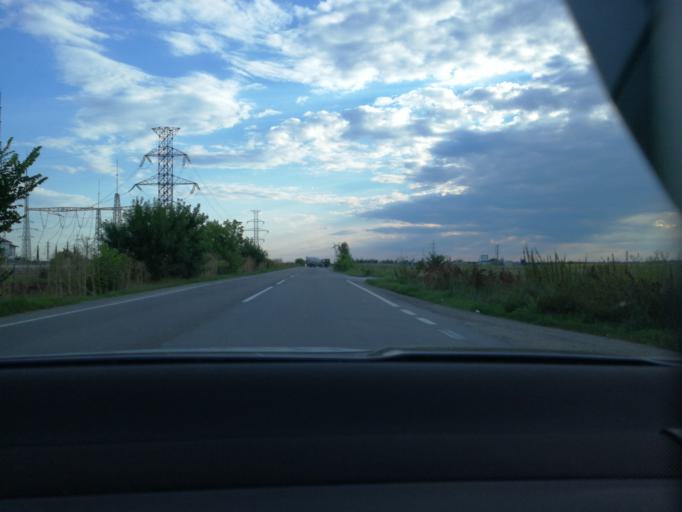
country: RO
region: Prahova
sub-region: Comuna Brazi
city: Negoiesti
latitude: 44.8987
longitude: 25.9721
